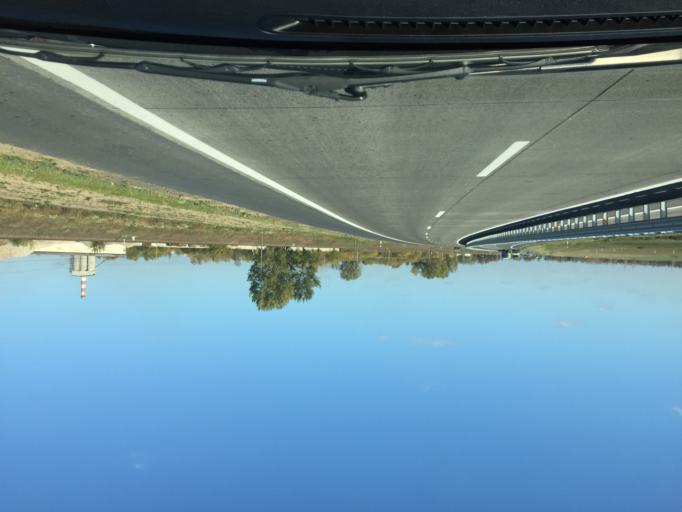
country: BY
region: Minsk
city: Slutsk
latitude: 52.9977
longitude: 27.5059
